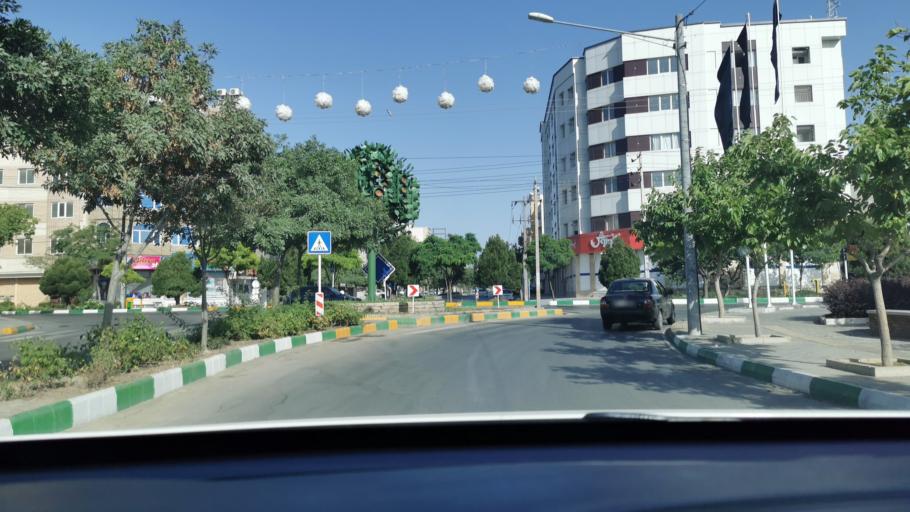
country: IR
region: Razavi Khorasan
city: Mashhad
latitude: 36.3386
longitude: 59.5074
